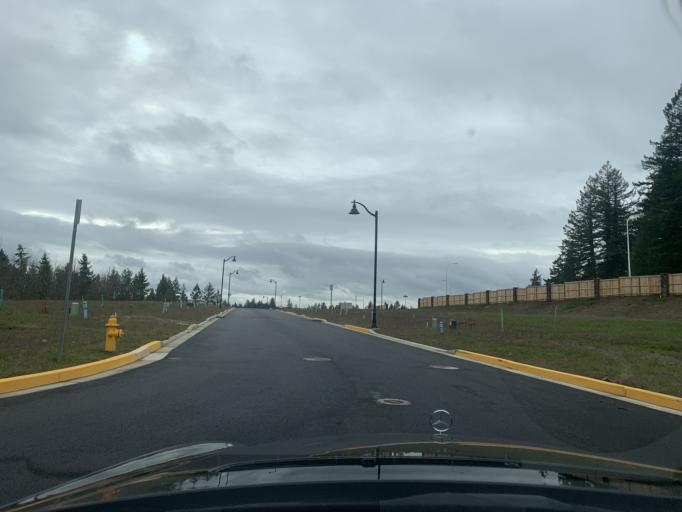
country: US
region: Oregon
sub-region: Clackamas County
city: Happy Valley
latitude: 45.4449
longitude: -122.5040
